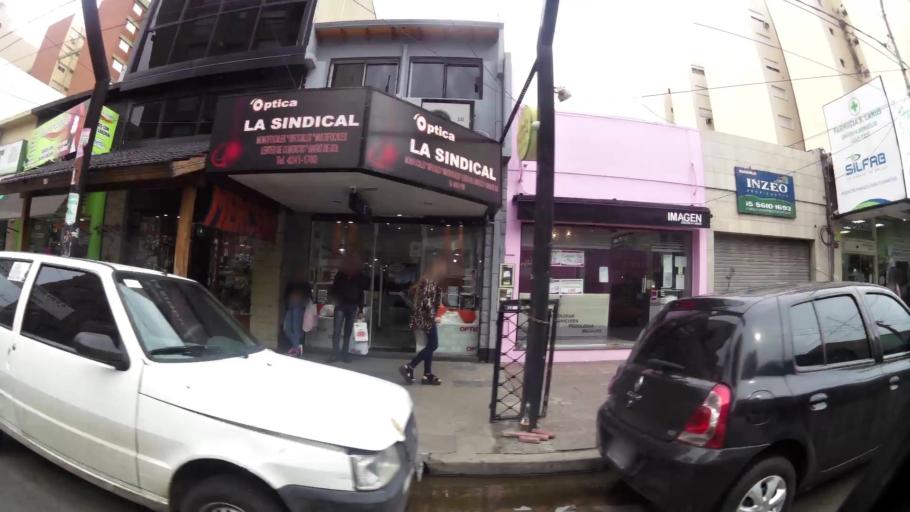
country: AR
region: Buenos Aires
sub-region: Partido de Lanus
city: Lanus
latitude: -34.7080
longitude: -58.3887
